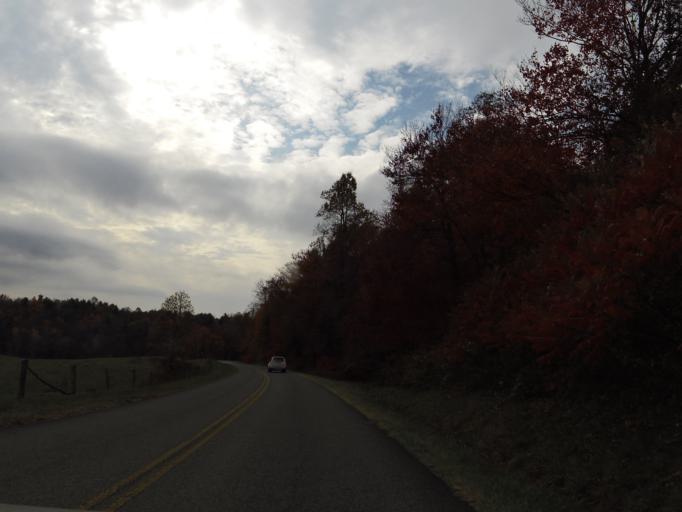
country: US
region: Virginia
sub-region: Carroll County
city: Woodlawn
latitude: 36.6069
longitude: -80.8122
